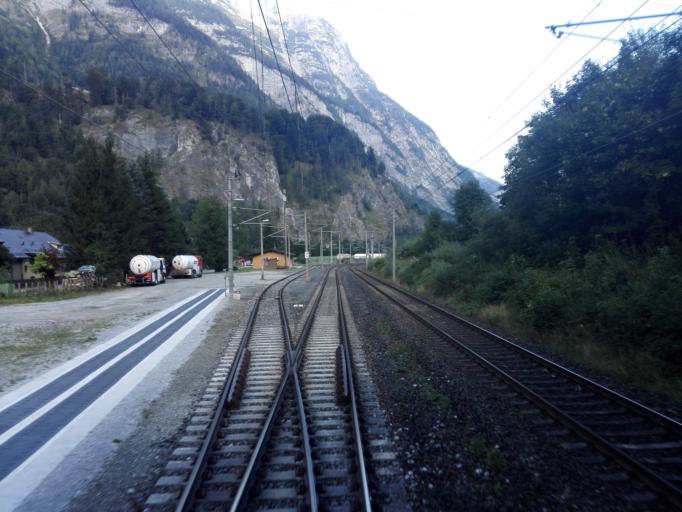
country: AT
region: Salzburg
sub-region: Politischer Bezirk Sankt Johann im Pongau
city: Werfen
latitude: 47.5227
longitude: 13.1670
